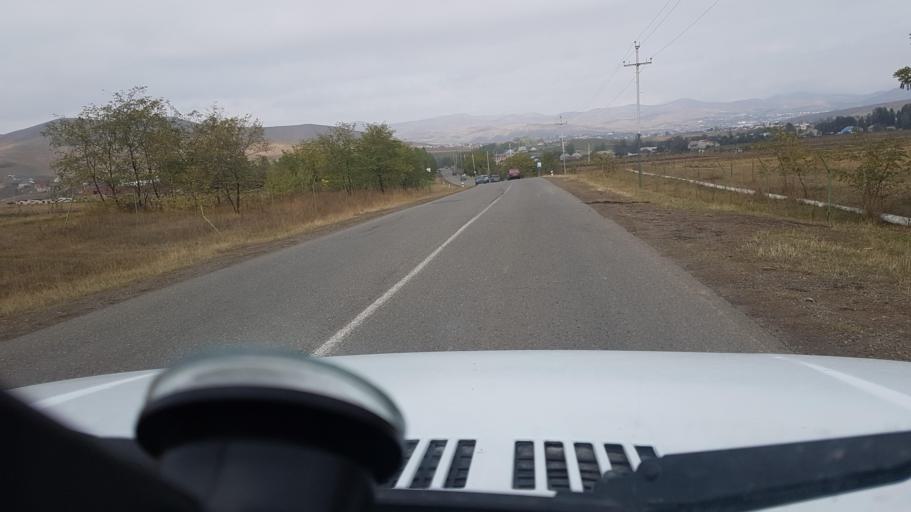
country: AZ
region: Gadabay Rayon
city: Ariqdam
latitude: 40.6259
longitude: 45.8169
